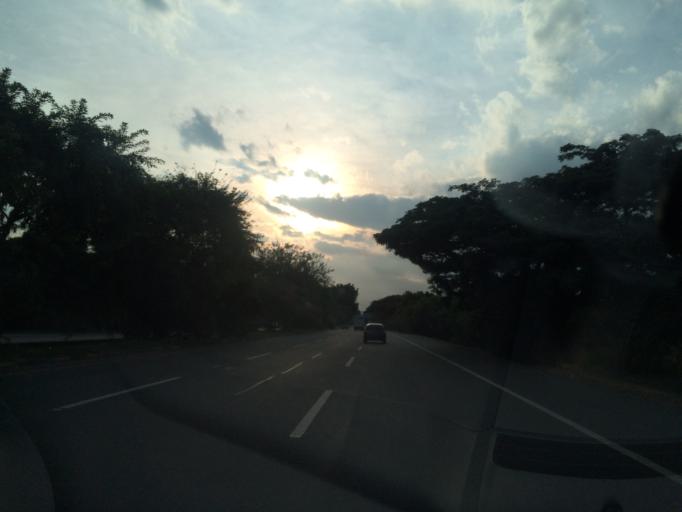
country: CO
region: Valle del Cauca
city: Yumbo
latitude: 3.5079
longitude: -76.4105
